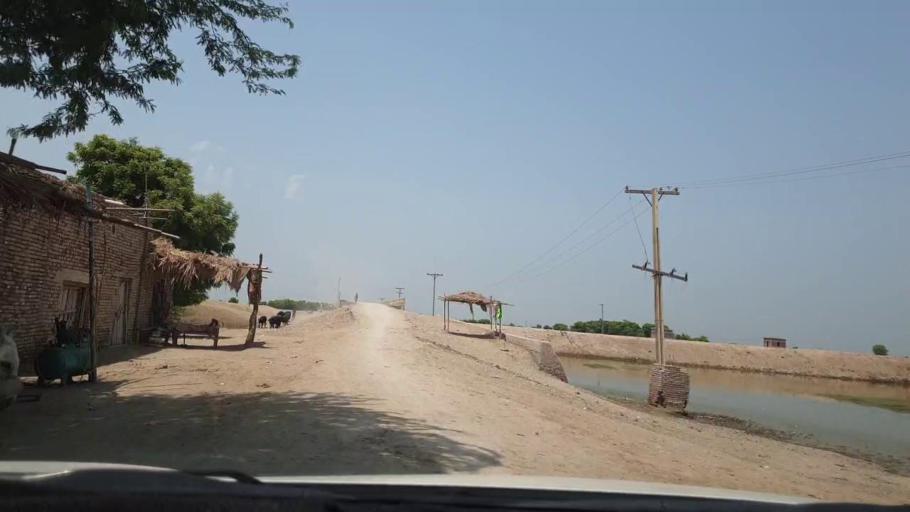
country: PK
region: Sindh
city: Radhan
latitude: 27.2465
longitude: 67.9873
